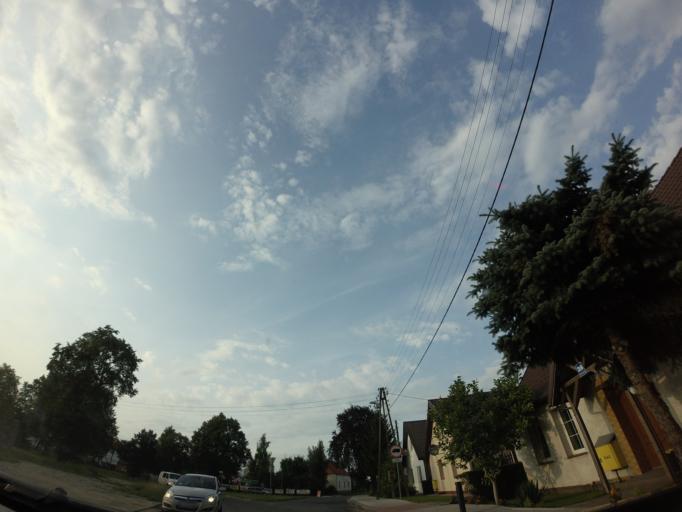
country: PL
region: West Pomeranian Voivodeship
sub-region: Powiat stargardzki
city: Stargard Szczecinski
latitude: 53.2974
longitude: 15.0497
